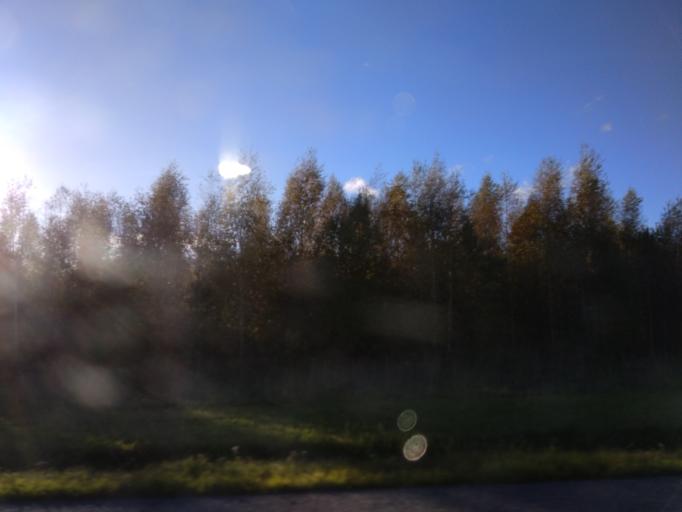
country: EE
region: Polvamaa
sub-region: Polva linn
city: Polva
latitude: 58.0237
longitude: 27.0635
